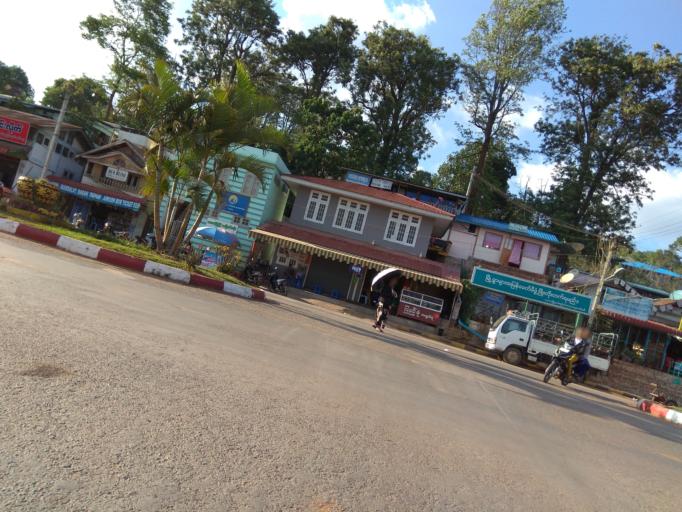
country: MM
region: Mandalay
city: Yamethin
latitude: 20.6360
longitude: 96.5664
